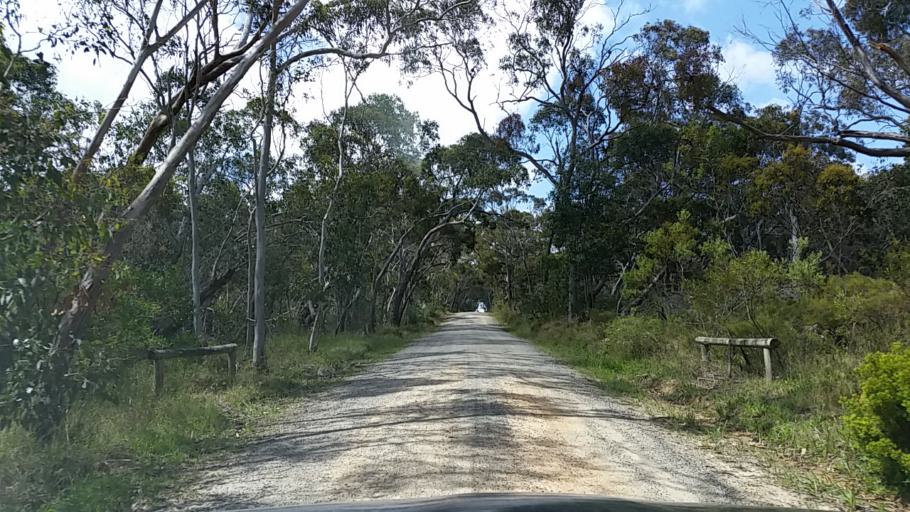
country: AU
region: South Australia
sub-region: Alexandrina
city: Mount Compass
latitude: -35.4399
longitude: 138.5825
